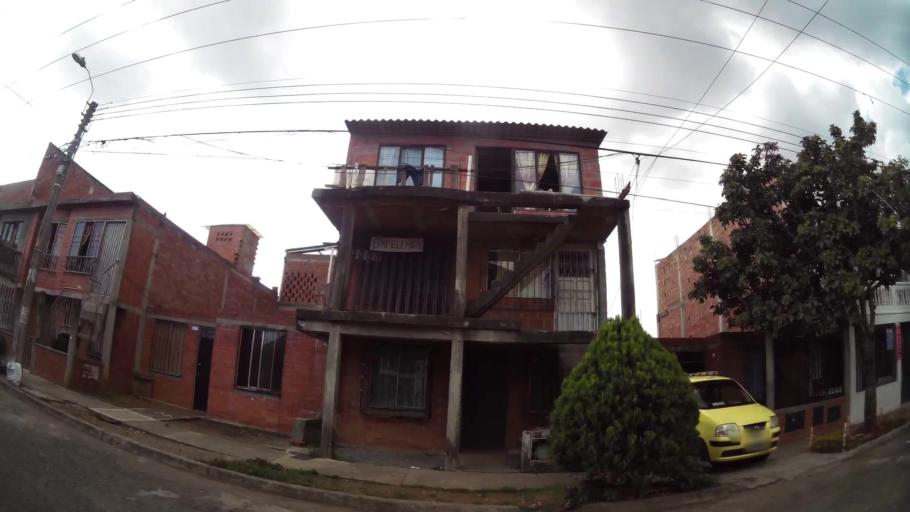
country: CO
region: Valle del Cauca
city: Cali
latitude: 3.4027
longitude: -76.5008
